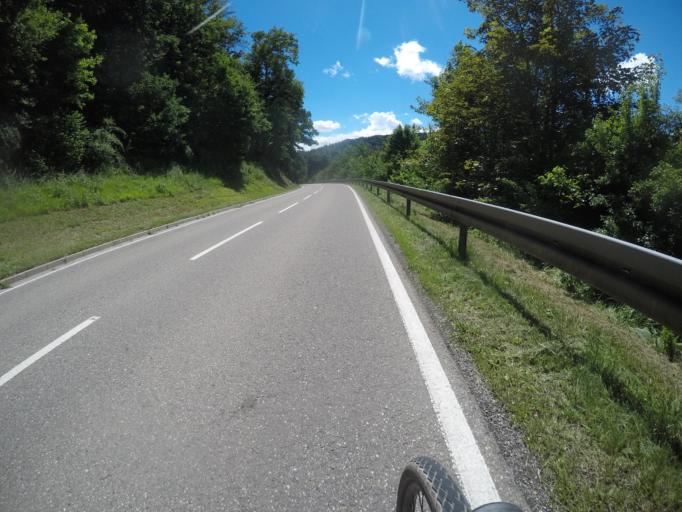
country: DE
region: Baden-Wuerttemberg
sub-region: Regierungsbezirk Stuttgart
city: Bondorf
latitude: 48.4474
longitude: 8.8169
